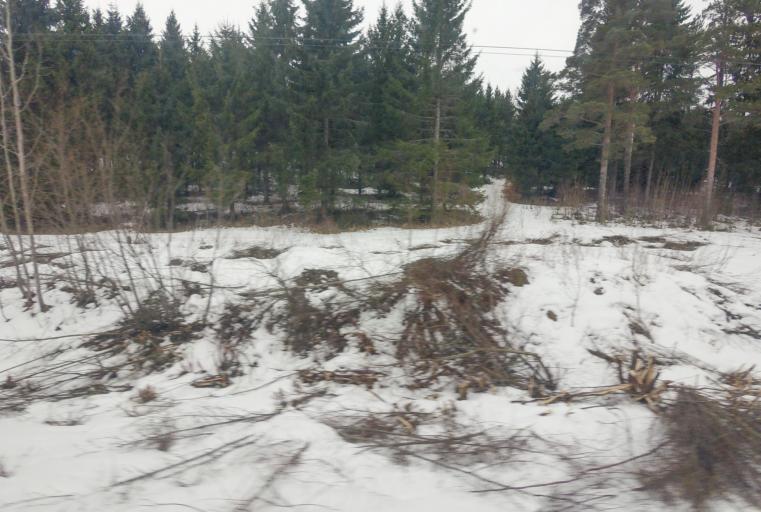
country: FI
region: South Karelia
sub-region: Imatra
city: Parikkala
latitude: 61.5834
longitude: 29.4933
